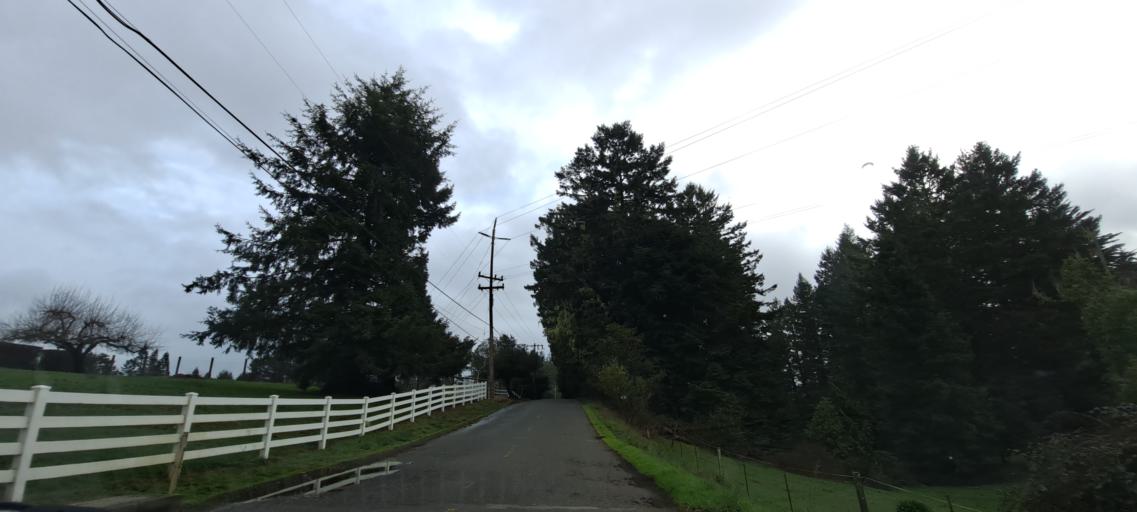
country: US
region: California
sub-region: Humboldt County
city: Fortuna
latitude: 40.6034
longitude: -124.1401
